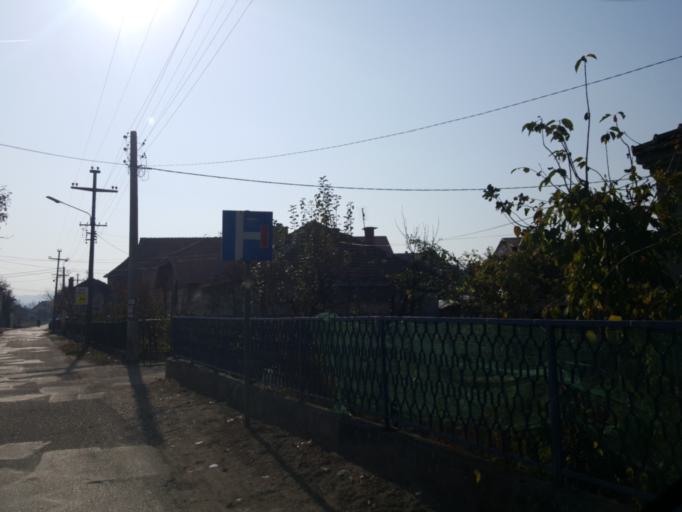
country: RS
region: Central Serbia
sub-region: Borski Okrug
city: Negotin
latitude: 44.2251
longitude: 22.5377
